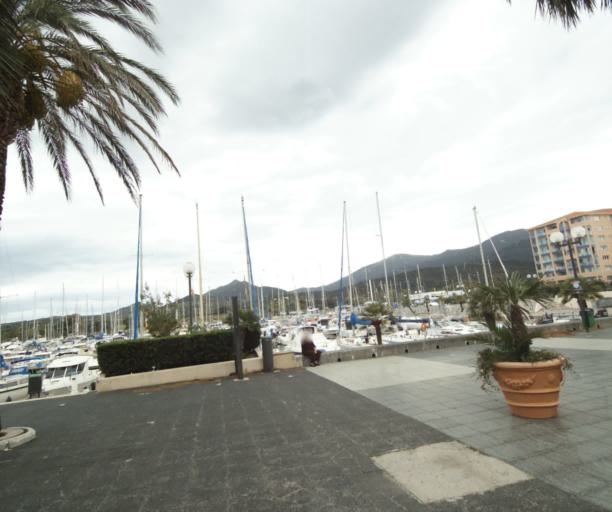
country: FR
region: Languedoc-Roussillon
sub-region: Departement des Pyrenees-Orientales
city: Argelers
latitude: 42.5422
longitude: 3.0485
